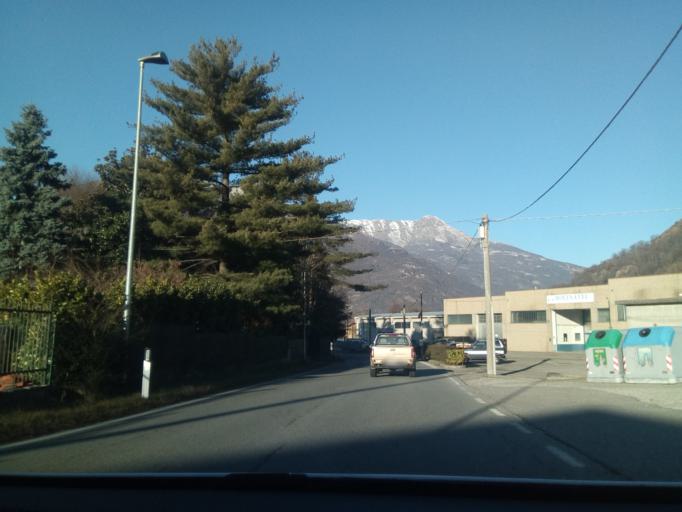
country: IT
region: Piedmont
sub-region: Provincia di Torino
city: Borgofranco d'Ivrea
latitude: 45.5154
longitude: 7.8658
